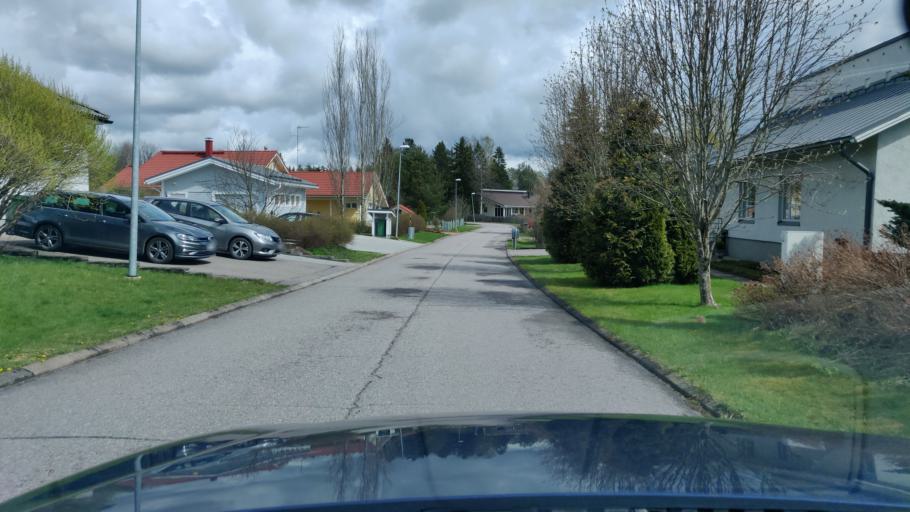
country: FI
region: Uusimaa
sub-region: Helsinki
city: Nurmijaervi
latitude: 60.3620
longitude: 24.7364
